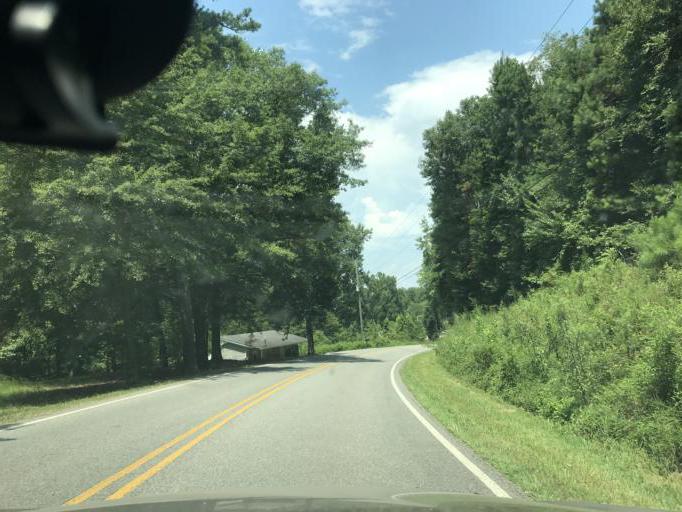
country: US
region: Georgia
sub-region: Forsyth County
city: Cumming
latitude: 34.3009
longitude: -84.1553
